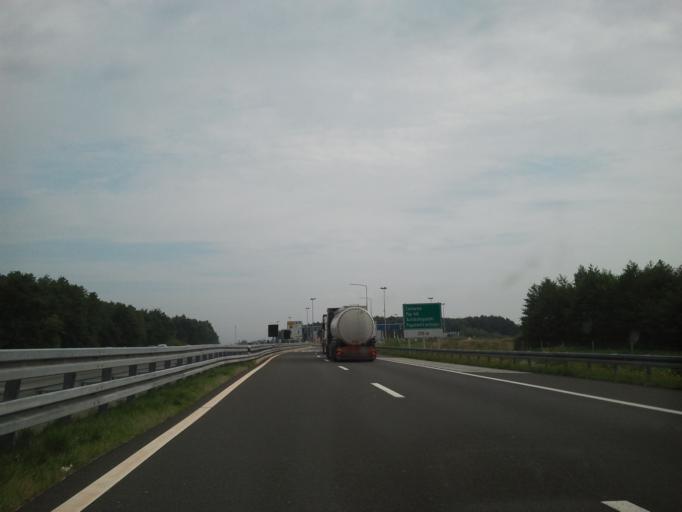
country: HR
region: Grad Zagreb
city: Brezovica
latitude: 45.7209
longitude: 15.8673
